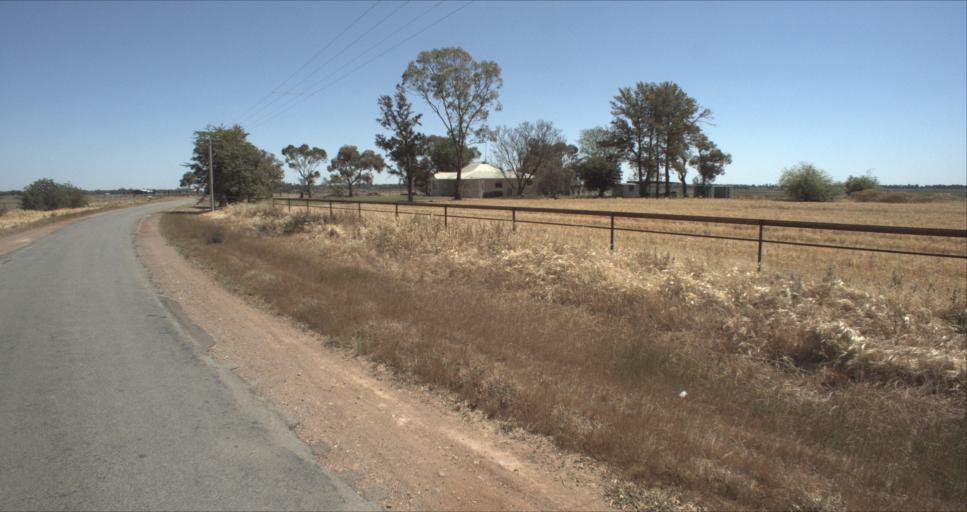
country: AU
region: New South Wales
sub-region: Leeton
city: Leeton
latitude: -34.5393
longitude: 146.4416
